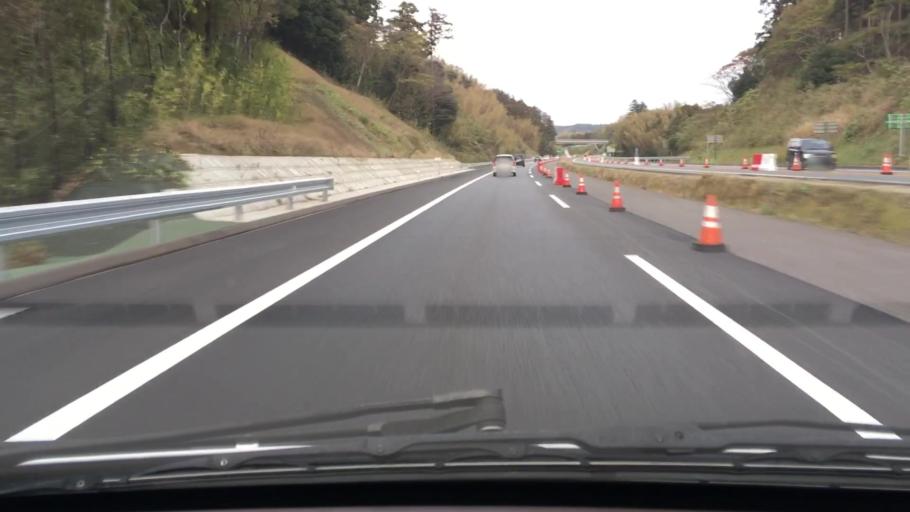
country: JP
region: Chiba
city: Kimitsu
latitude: 35.2955
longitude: 139.9336
